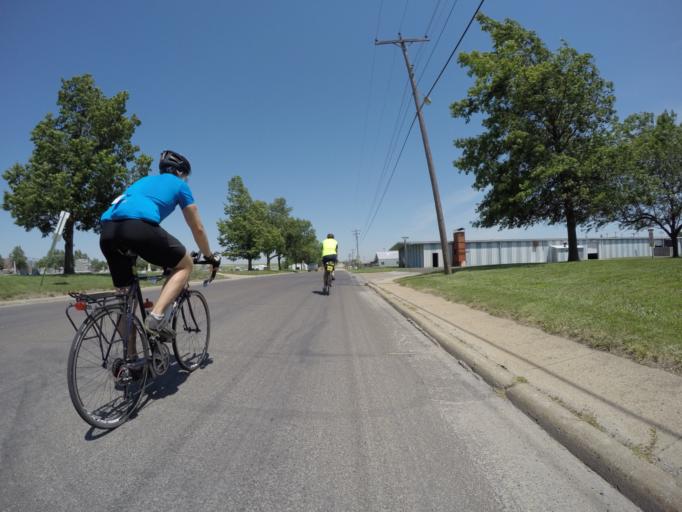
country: US
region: Kansas
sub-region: Nemaha County
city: Sabetha
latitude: 39.8997
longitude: -95.7907
